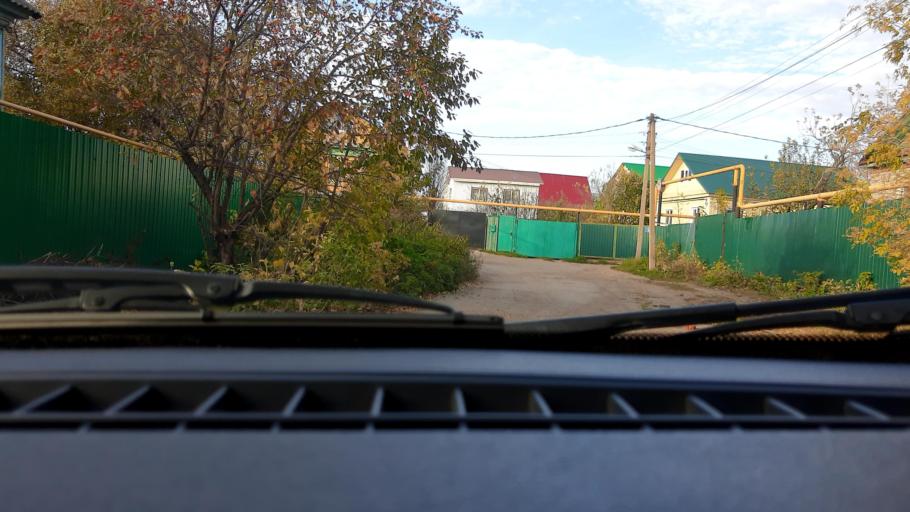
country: RU
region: Bashkortostan
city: Ufa
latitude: 54.7330
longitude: 55.8991
